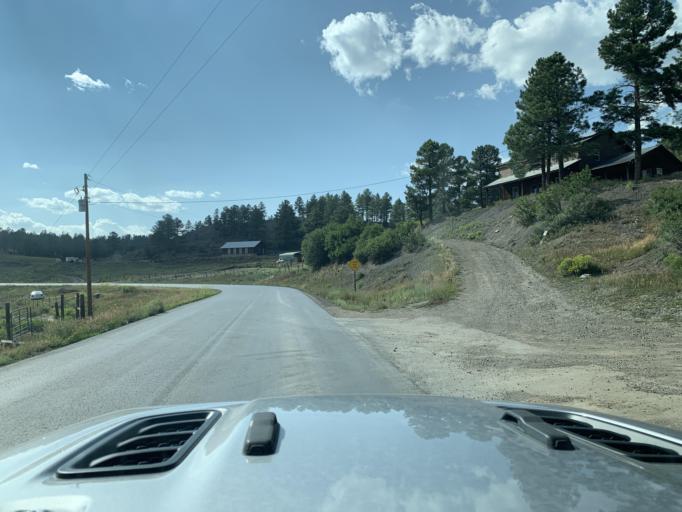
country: US
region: Colorado
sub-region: Archuleta County
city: Pagosa Springs
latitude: 37.2583
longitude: -107.0218
